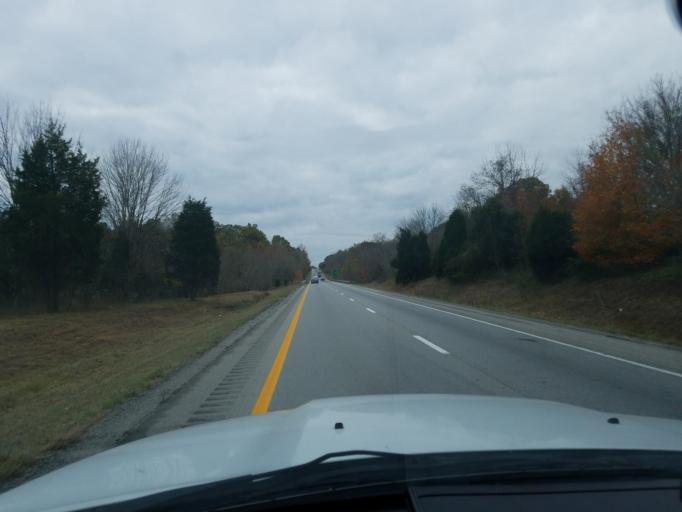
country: US
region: Kentucky
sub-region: Oldham County
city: La Grange
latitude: 38.4206
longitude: -85.3352
